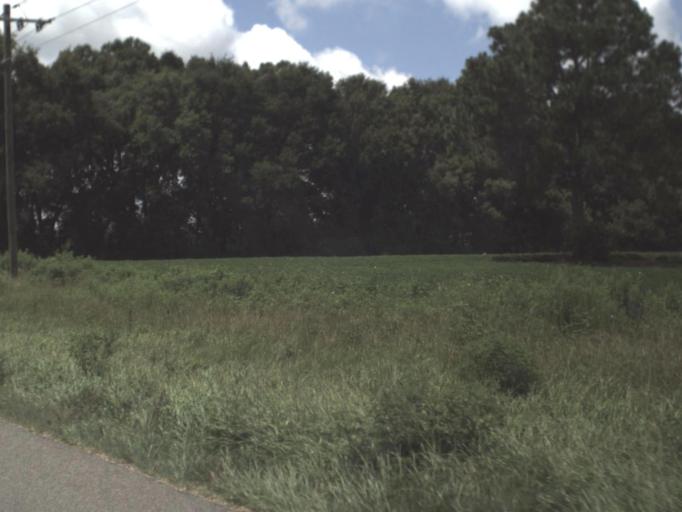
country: US
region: Florida
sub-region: Gilchrist County
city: Trenton
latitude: 29.6840
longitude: -82.8573
